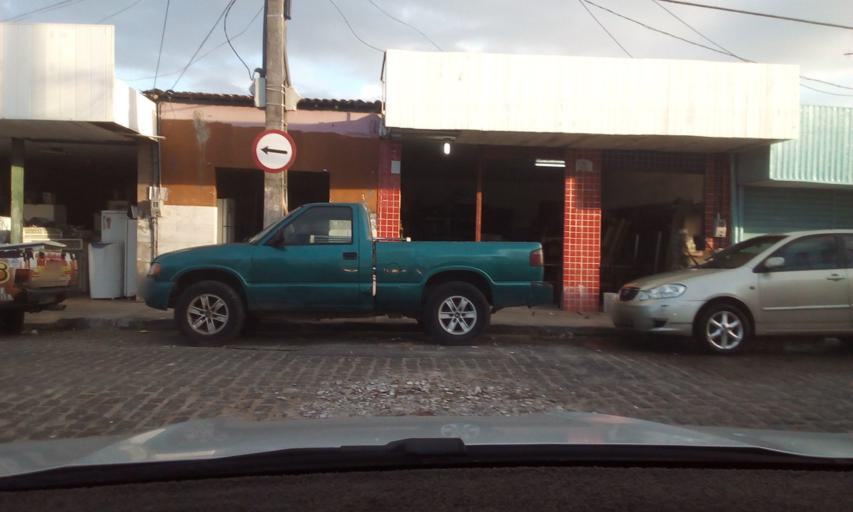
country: BR
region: Paraiba
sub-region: Joao Pessoa
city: Joao Pessoa
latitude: -7.1661
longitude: -34.8394
